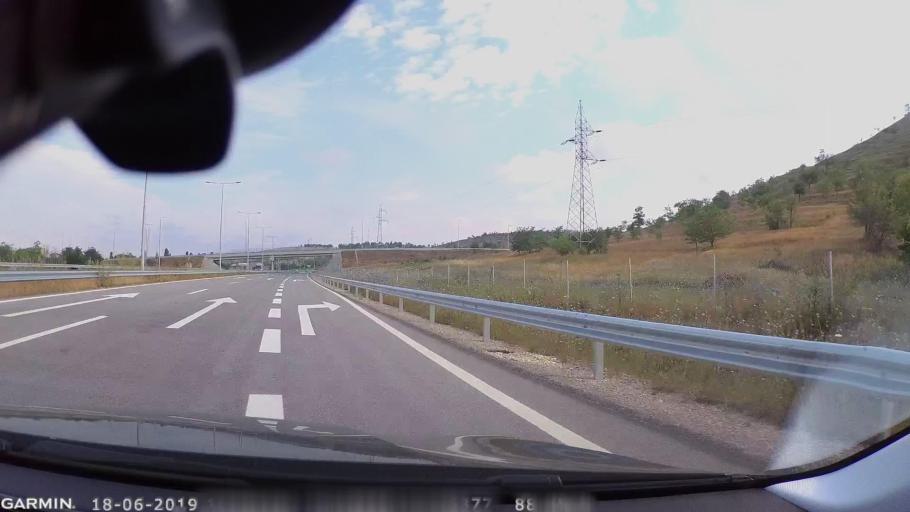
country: MK
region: Sveti Nikole
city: Sveti Nikole
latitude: 41.8544
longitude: 21.9635
